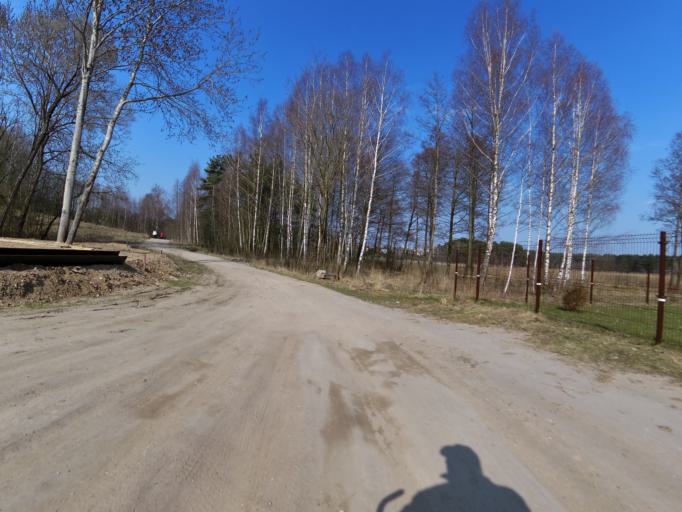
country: LT
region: Vilnius County
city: Pilaite
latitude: 54.6946
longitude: 25.1734
